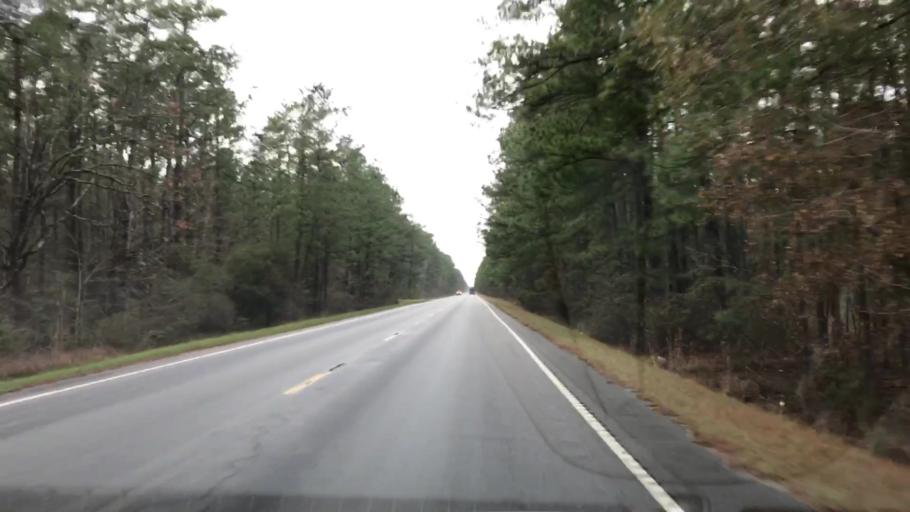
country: US
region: South Carolina
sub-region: Berkeley County
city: Saint Stephen
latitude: 33.2879
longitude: -79.8319
